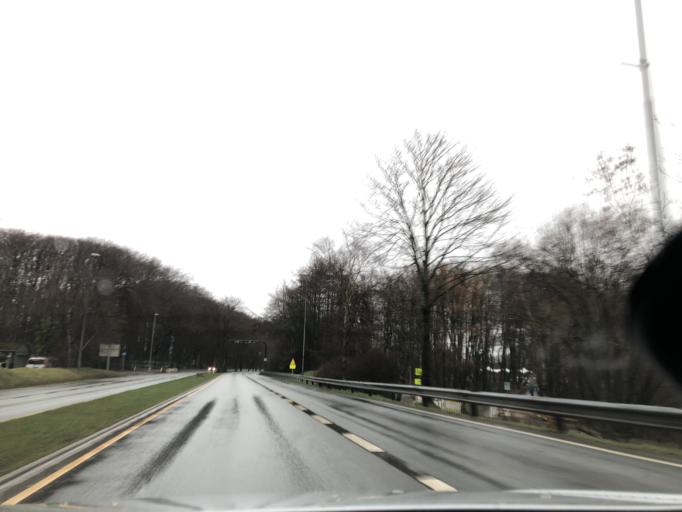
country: NO
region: Rogaland
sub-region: Stavanger
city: Stavanger
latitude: 58.9583
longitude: 5.7049
